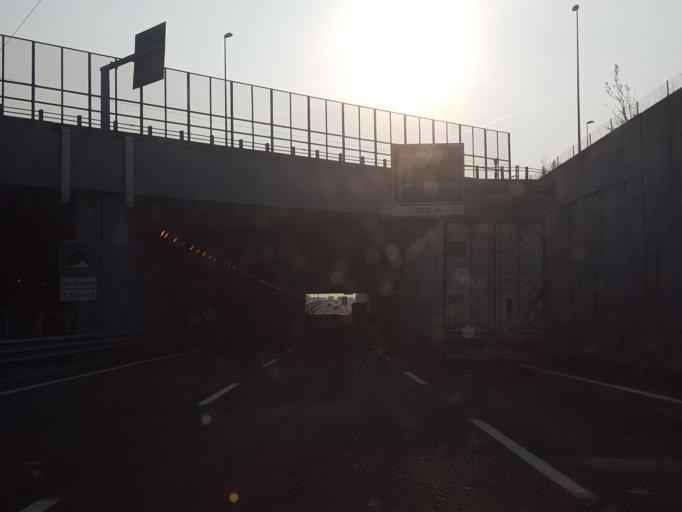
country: IT
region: Veneto
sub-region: Provincia di Venezia
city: Scaltenigo
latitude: 45.4591
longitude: 12.0960
